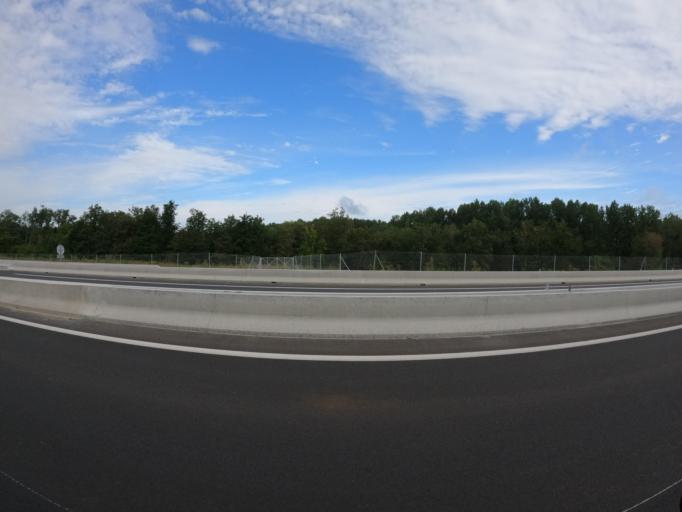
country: FR
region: Centre
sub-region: Departement d'Indre-et-Loire
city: Langeais
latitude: 47.3349
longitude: 0.3492
